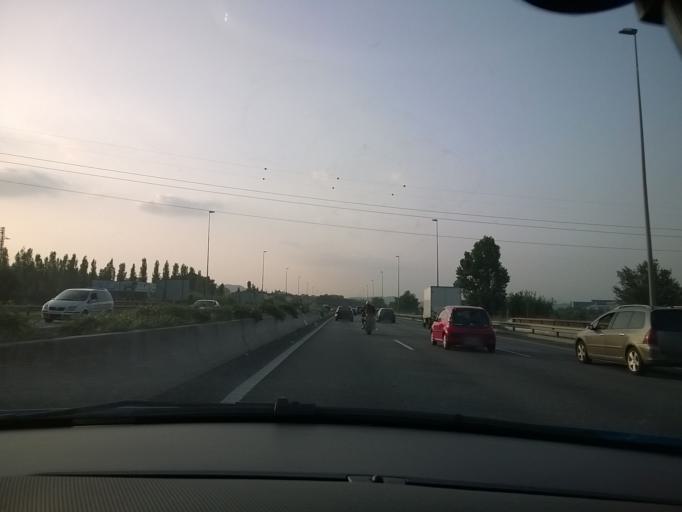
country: ES
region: Catalonia
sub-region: Provincia de Barcelona
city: Sant Andreu de la Barca
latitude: 41.4432
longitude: 1.9837
